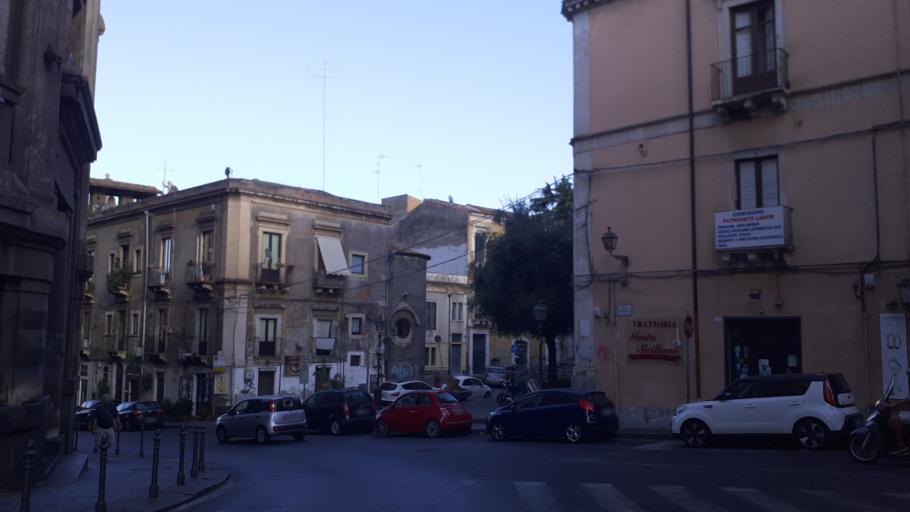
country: IT
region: Sicily
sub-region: Catania
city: Catania
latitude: 37.5075
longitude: 15.0838
